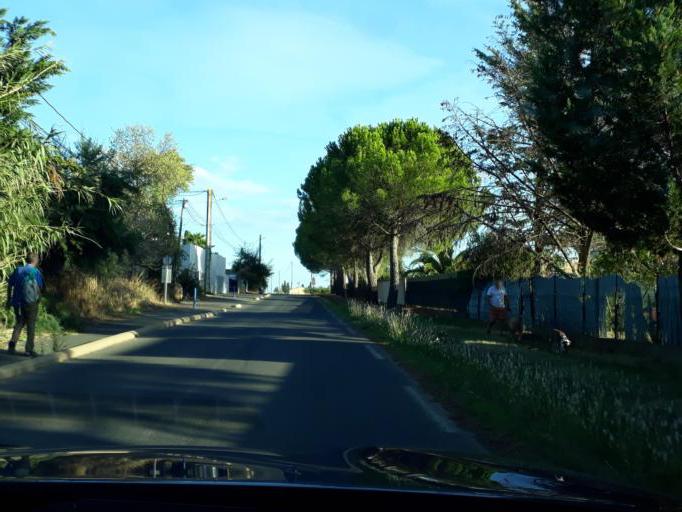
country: FR
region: Languedoc-Roussillon
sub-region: Departement de l'Herault
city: Pomerols
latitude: 43.3881
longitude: 3.5015
